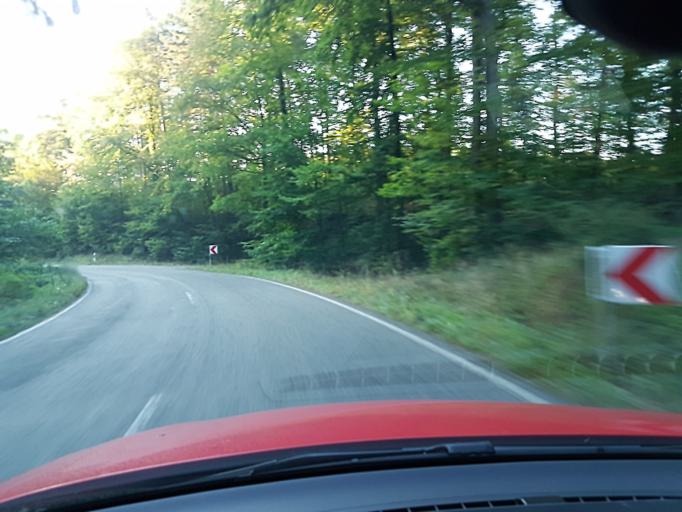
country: DE
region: Baden-Wuerttemberg
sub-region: Regierungsbezirk Stuttgart
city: Zaberfeld
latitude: 49.0905
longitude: 8.9052
